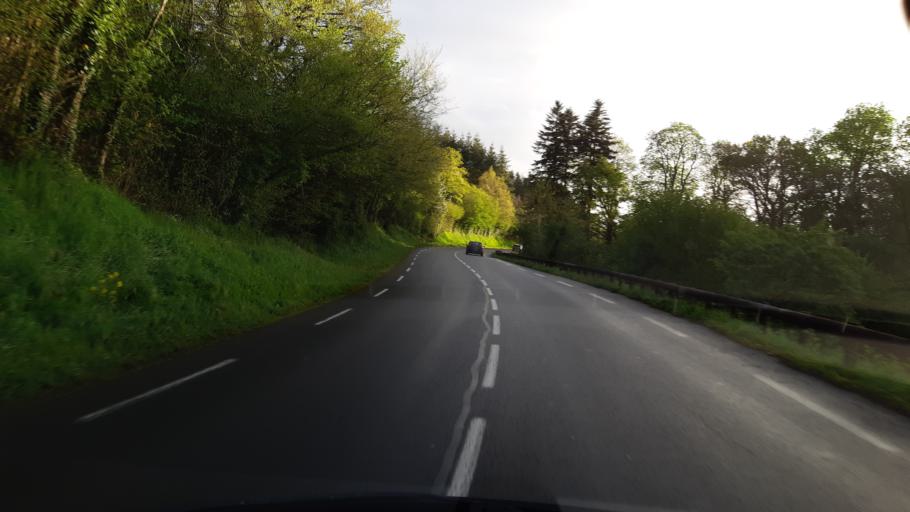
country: FR
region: Lower Normandy
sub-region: Departement de la Manche
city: Agneaux
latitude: 49.0792
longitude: -1.1213
